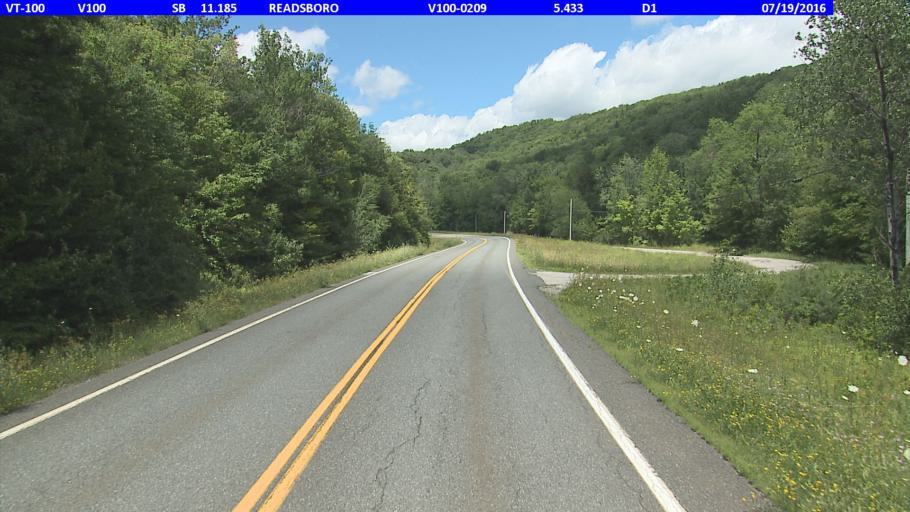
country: US
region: Massachusetts
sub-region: Berkshire County
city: North Adams
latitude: 42.7887
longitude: -72.9614
